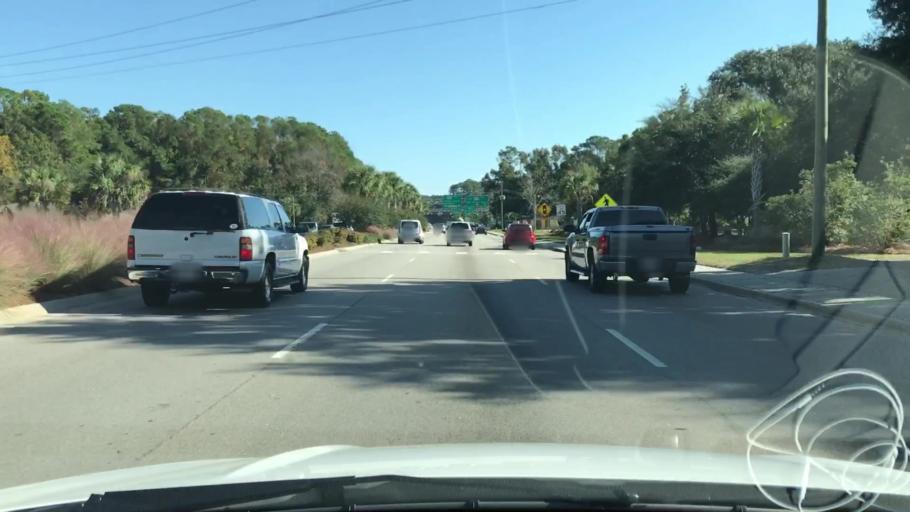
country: US
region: South Carolina
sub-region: Beaufort County
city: Hilton Head Island
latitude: 32.2161
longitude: -80.7512
